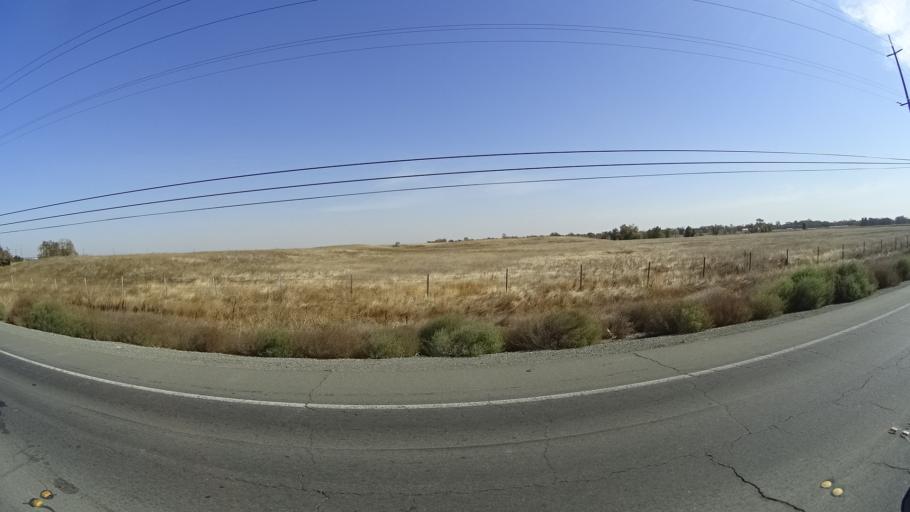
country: US
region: California
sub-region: Yolo County
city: Woodland
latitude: 38.6451
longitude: -121.7292
